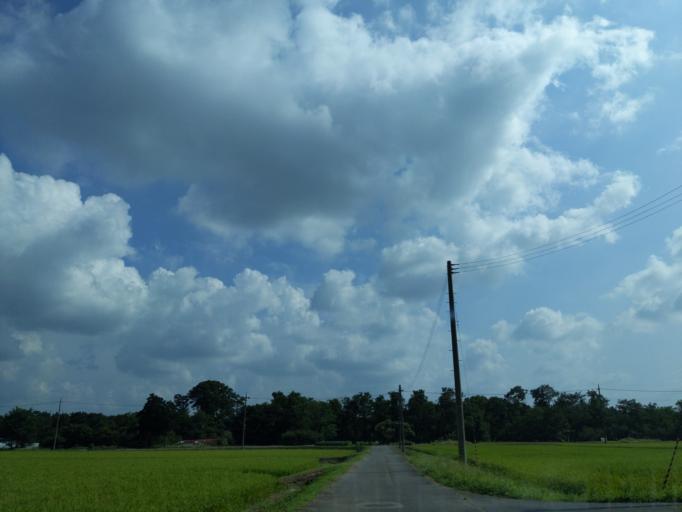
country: JP
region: Fukushima
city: Koriyama
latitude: 37.3588
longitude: 140.3229
